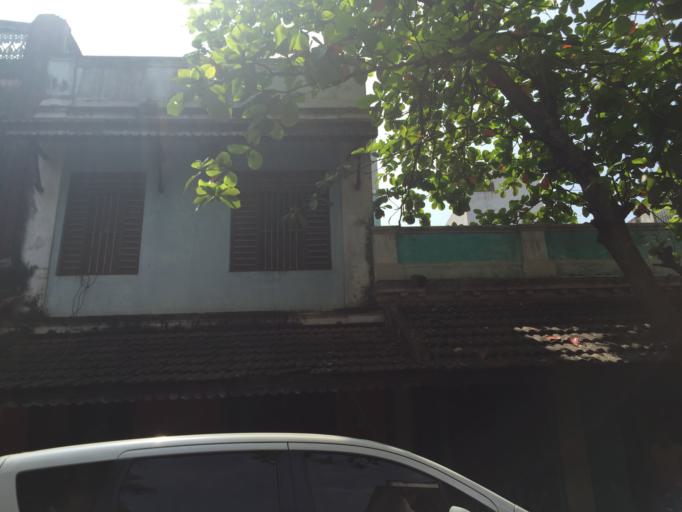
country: IN
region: Pondicherry
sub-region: Puducherry
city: Puducherry
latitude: 11.9378
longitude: 79.8302
